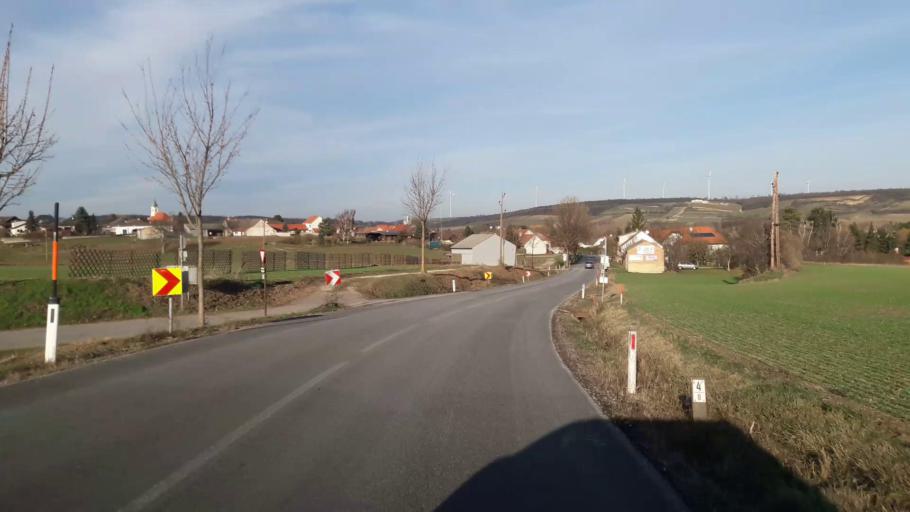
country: AT
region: Lower Austria
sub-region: Politischer Bezirk Ganserndorf
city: Gross-Schweinbarth
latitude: 48.4074
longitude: 16.6340
